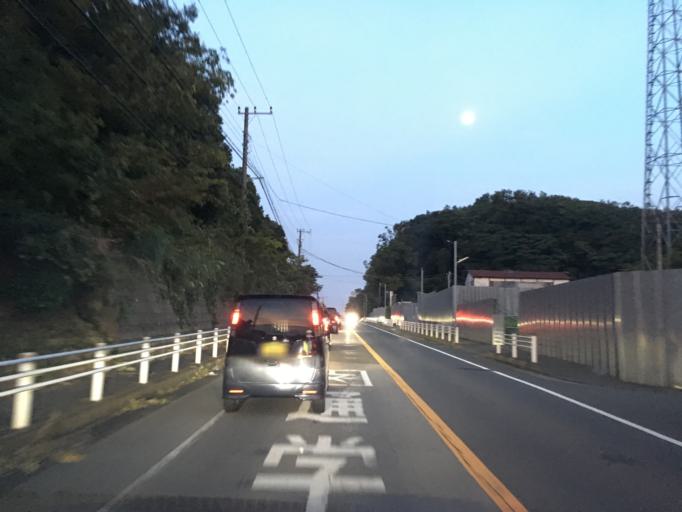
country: JP
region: Chiba
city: Kisarazu
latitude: 35.3458
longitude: 139.9165
